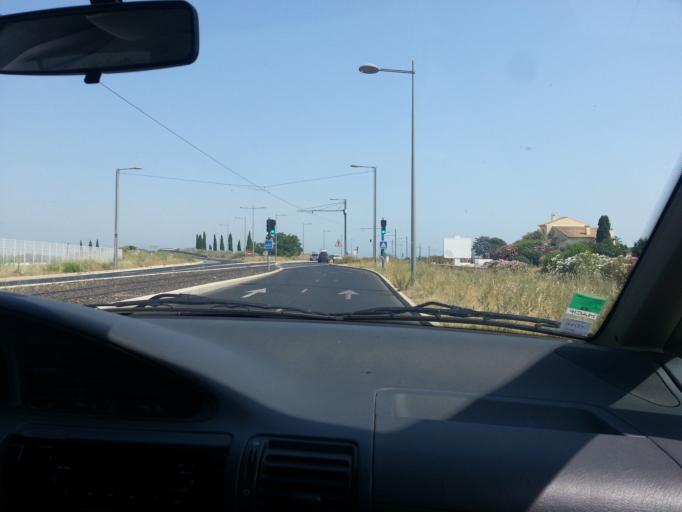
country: FR
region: Languedoc-Roussillon
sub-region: Departement de l'Herault
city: Perols
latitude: 43.5691
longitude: 3.9534
